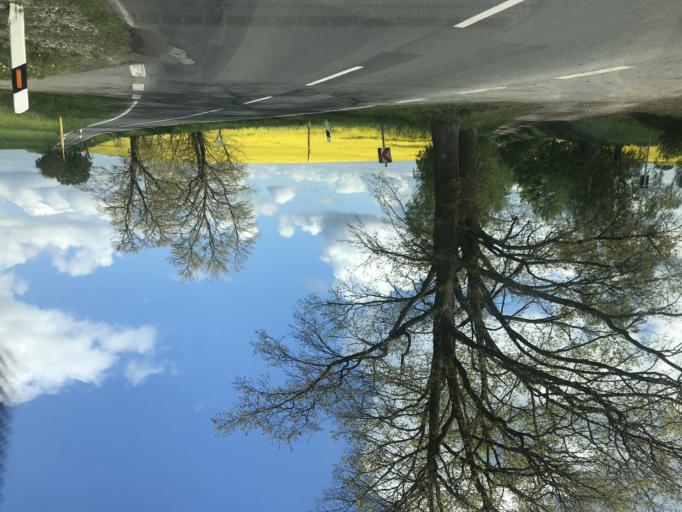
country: DE
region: Brandenburg
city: Gransee
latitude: 52.9385
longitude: 13.1721
